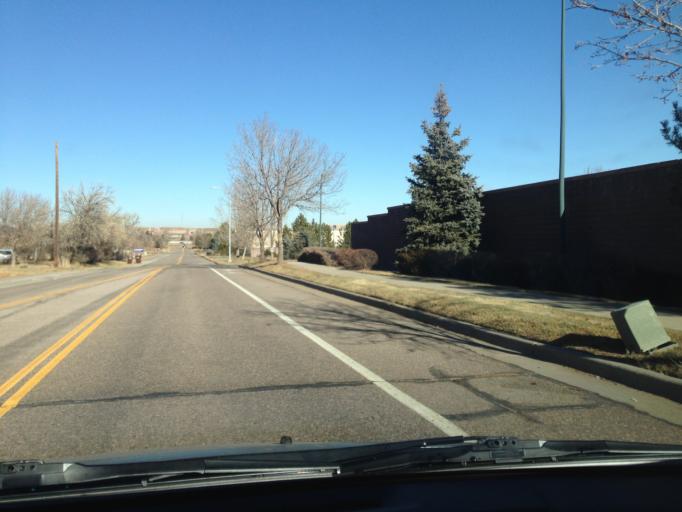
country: US
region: Colorado
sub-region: Boulder County
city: Superior
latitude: 39.9569
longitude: -105.1752
